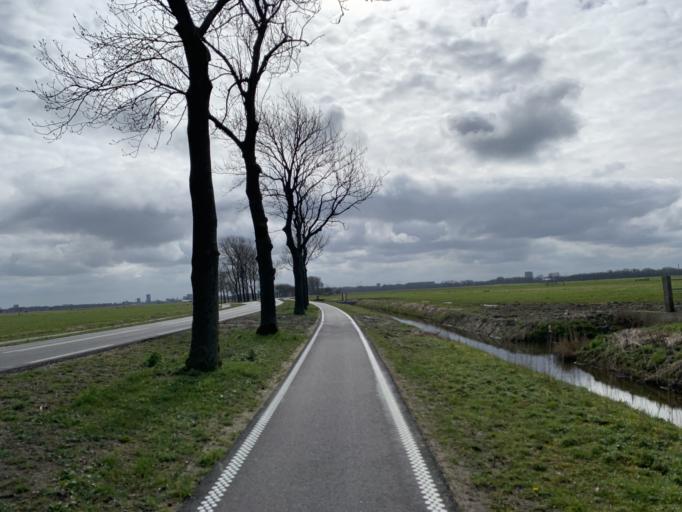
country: NL
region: Groningen
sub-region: Gemeente Groningen
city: Korrewegwijk
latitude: 53.2655
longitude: 6.5368
